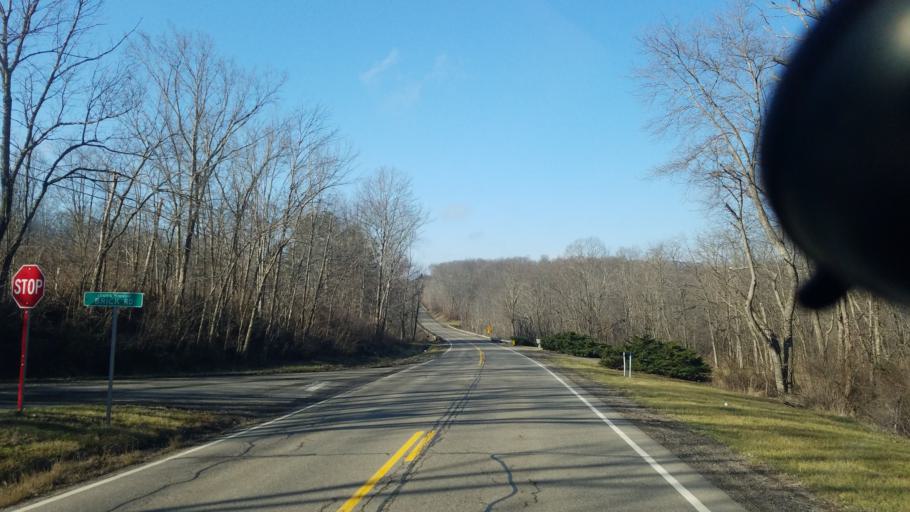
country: US
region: Ohio
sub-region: Guernsey County
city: Byesville
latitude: 40.0384
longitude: -81.4681
